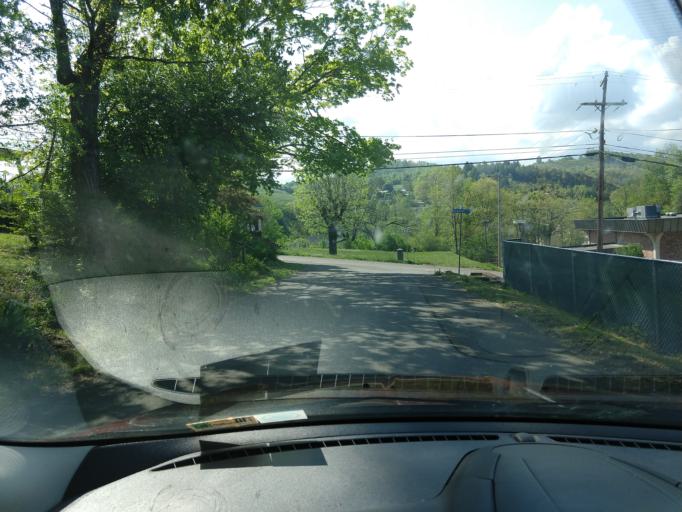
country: US
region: Virginia
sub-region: Russell County
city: Honaker
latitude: 37.0173
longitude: -81.9705
